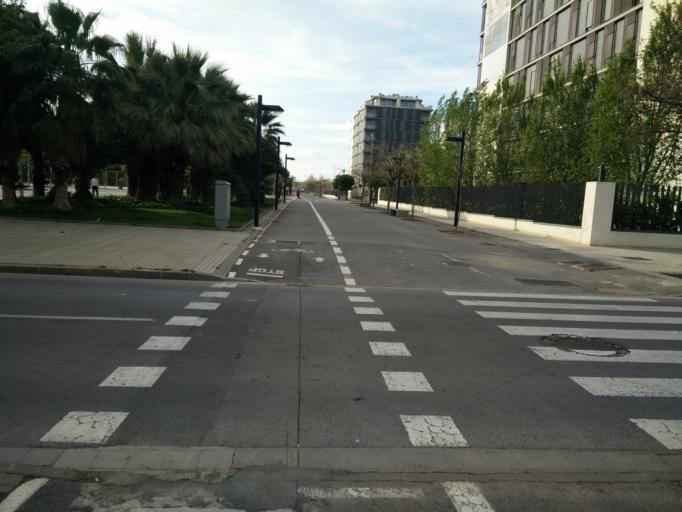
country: ES
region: Valencia
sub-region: Provincia de Castello
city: Castello de la Plana
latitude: 39.9781
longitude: -0.0573
